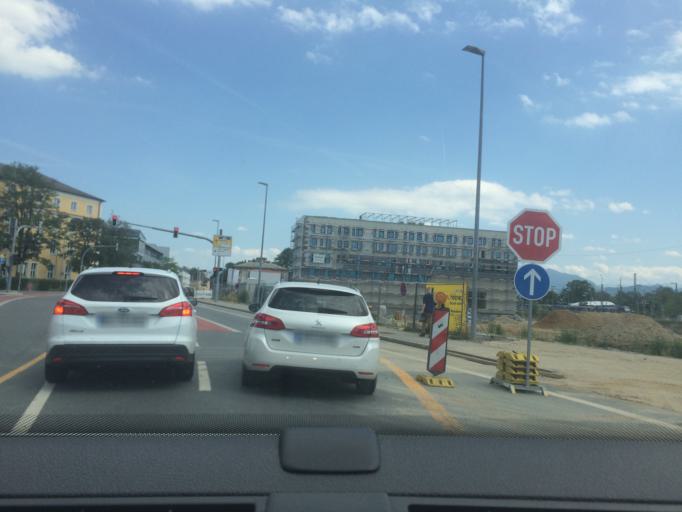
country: DE
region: Bavaria
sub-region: Upper Bavaria
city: Rosenheim
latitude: 47.8521
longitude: 12.1161
